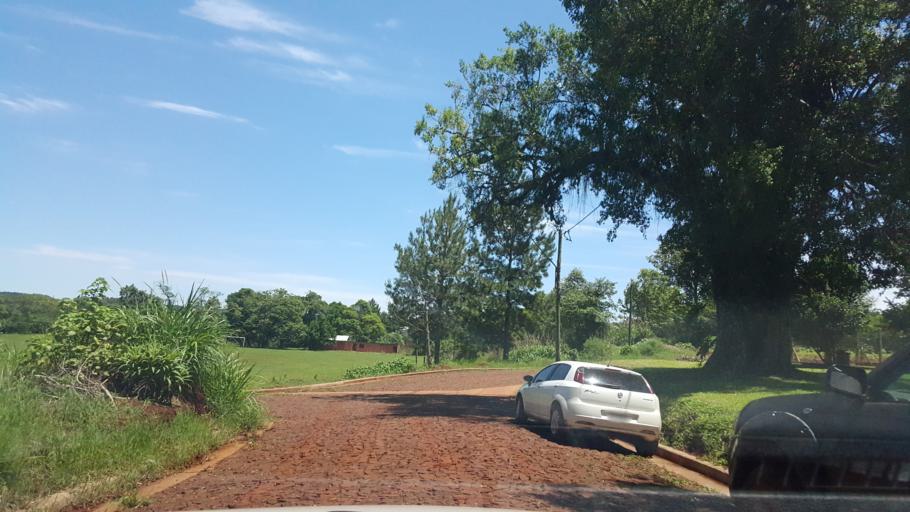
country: AR
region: Misiones
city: Capiovi
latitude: -26.9359
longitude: -55.0610
